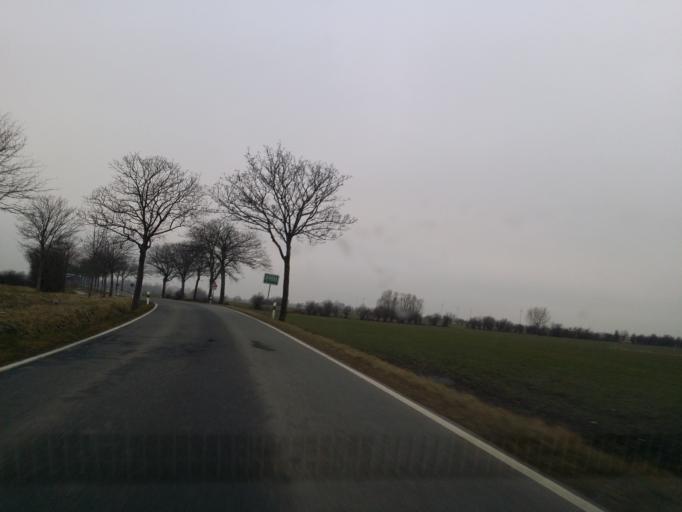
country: DE
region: Schleswig-Holstein
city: Fehmarn
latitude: 54.4562
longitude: 11.1364
